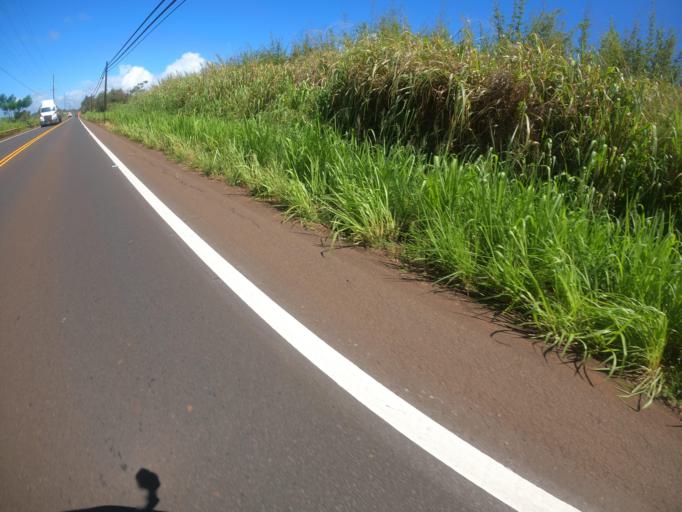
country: US
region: Hawaii
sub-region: Honolulu County
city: Schofield Barracks
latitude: 21.4650
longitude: -158.0552
